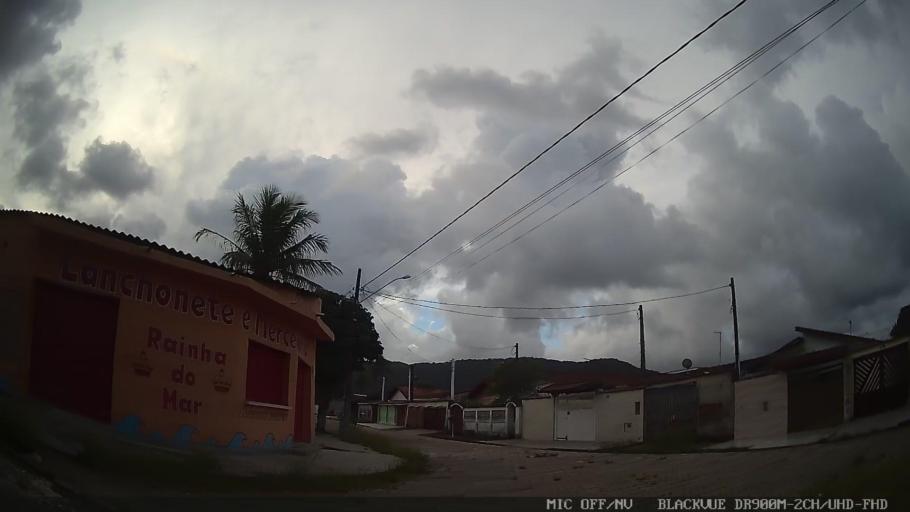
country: BR
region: Sao Paulo
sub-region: Itanhaem
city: Itanhaem
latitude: -24.1527
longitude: -46.7331
